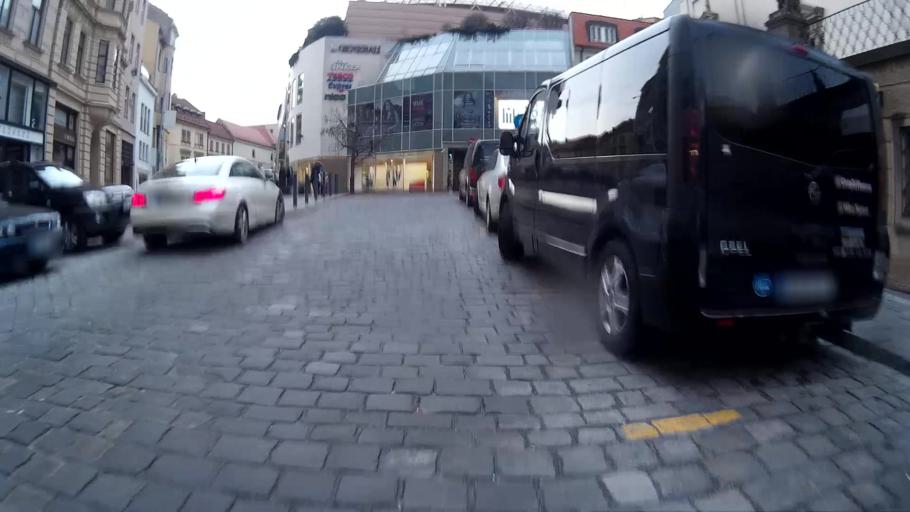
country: CZ
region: South Moravian
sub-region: Mesto Brno
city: Brno
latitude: 49.1939
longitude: 16.6071
